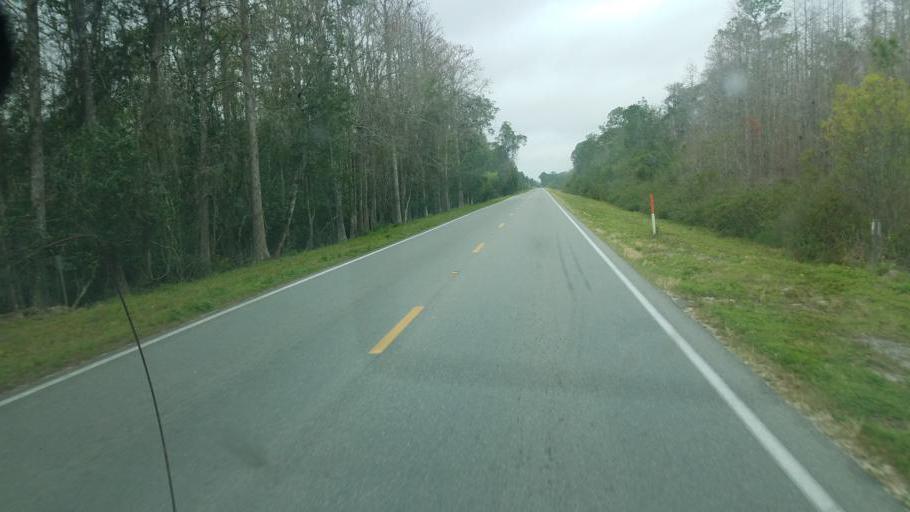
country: US
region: Florida
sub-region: Polk County
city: Polk City
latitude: 28.2589
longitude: -81.7746
